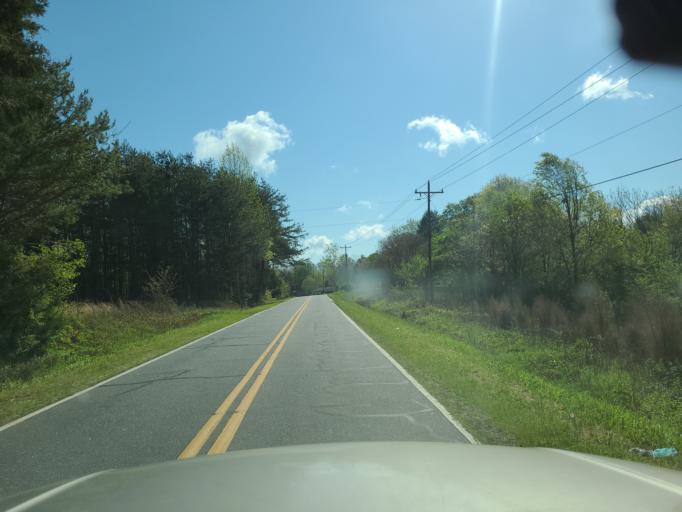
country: US
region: North Carolina
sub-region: Rutherford County
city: Spindale
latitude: 35.2958
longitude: -81.9540
